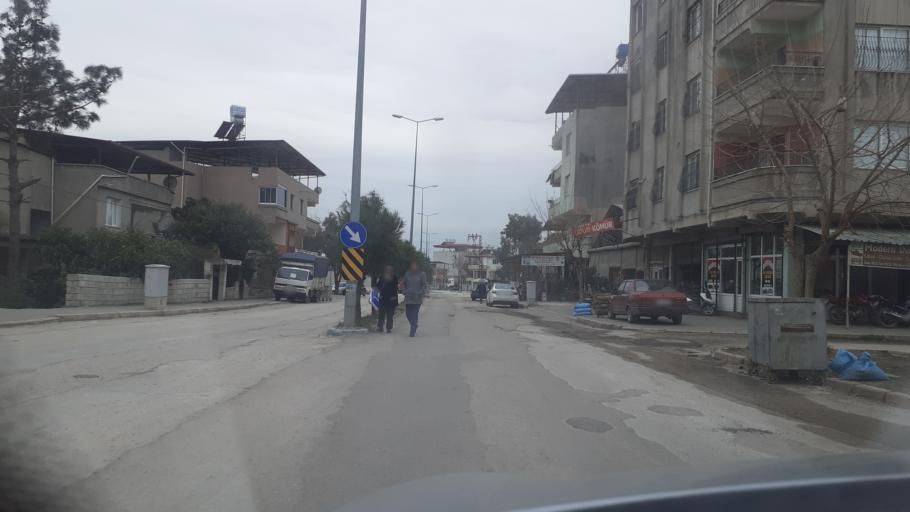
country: TR
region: Hatay
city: Kirikhan
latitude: 36.4930
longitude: 36.3582
